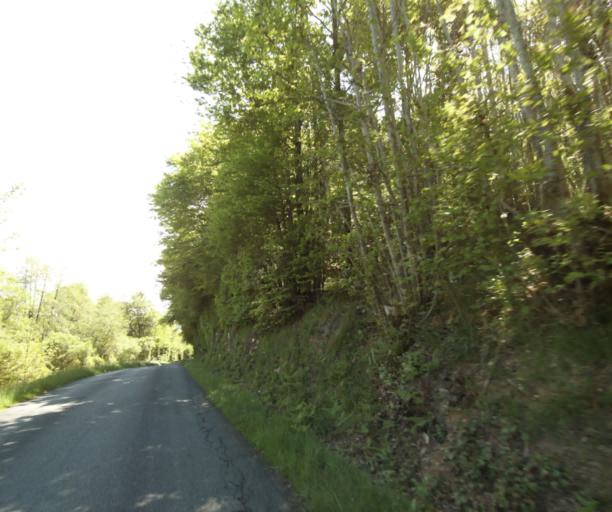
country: FR
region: Poitou-Charentes
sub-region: Departement de la Charente-Maritime
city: Chaniers
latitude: 45.7454
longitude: -0.5086
